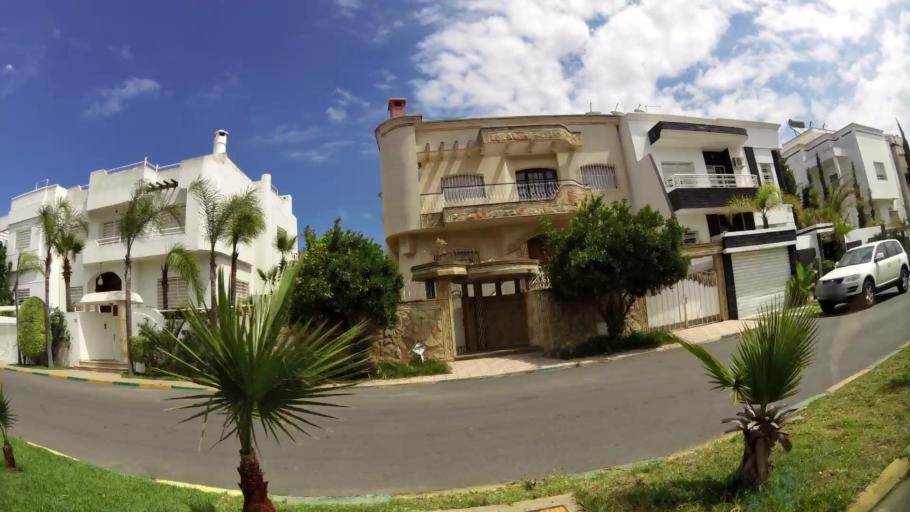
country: MA
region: Gharb-Chrarda-Beni Hssen
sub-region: Kenitra Province
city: Kenitra
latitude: 34.2429
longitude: -6.6023
